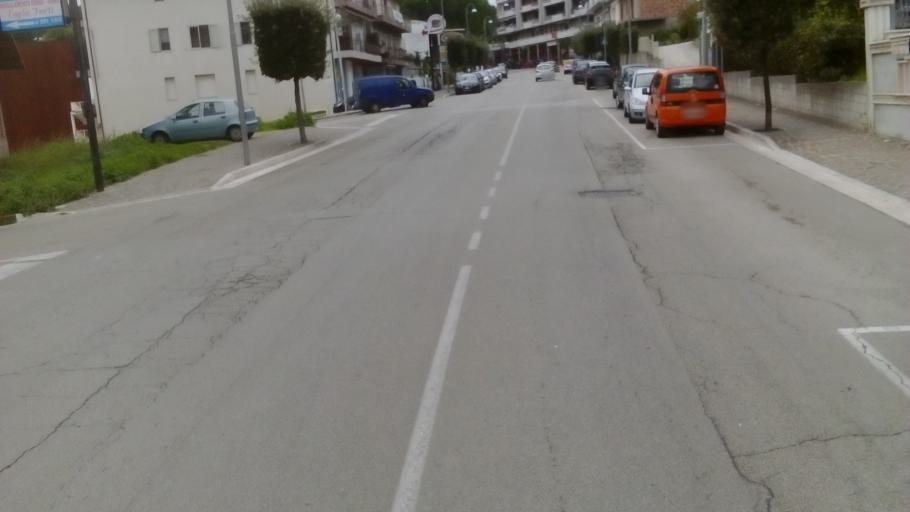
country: IT
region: Abruzzo
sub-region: Provincia di Chieti
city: San Salvo
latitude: 42.0510
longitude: 14.7318
